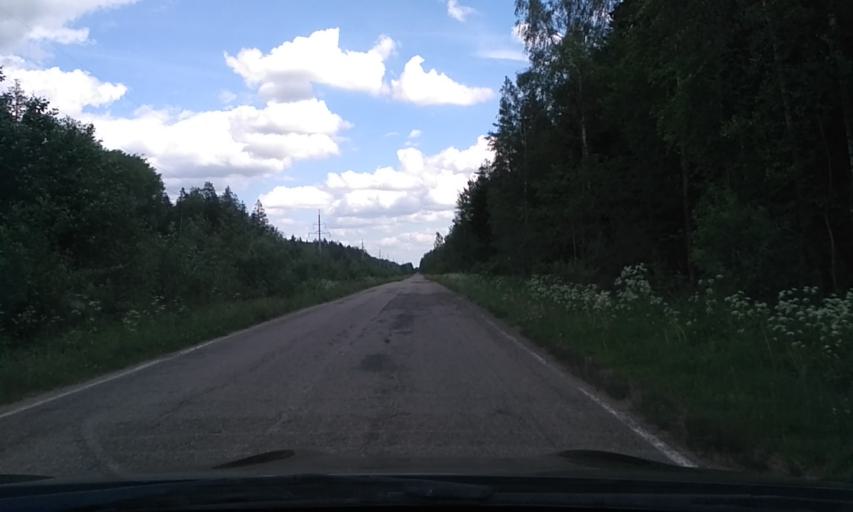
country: RU
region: Leningrad
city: Otradnoye
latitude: 59.8208
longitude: 30.7901
